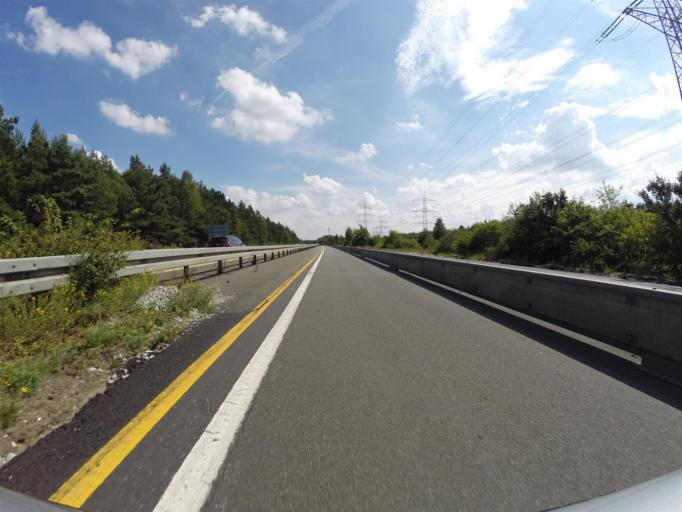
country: DE
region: North Rhine-Westphalia
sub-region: Regierungsbezirk Detmold
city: Hovelhof
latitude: 51.8376
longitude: 8.6857
